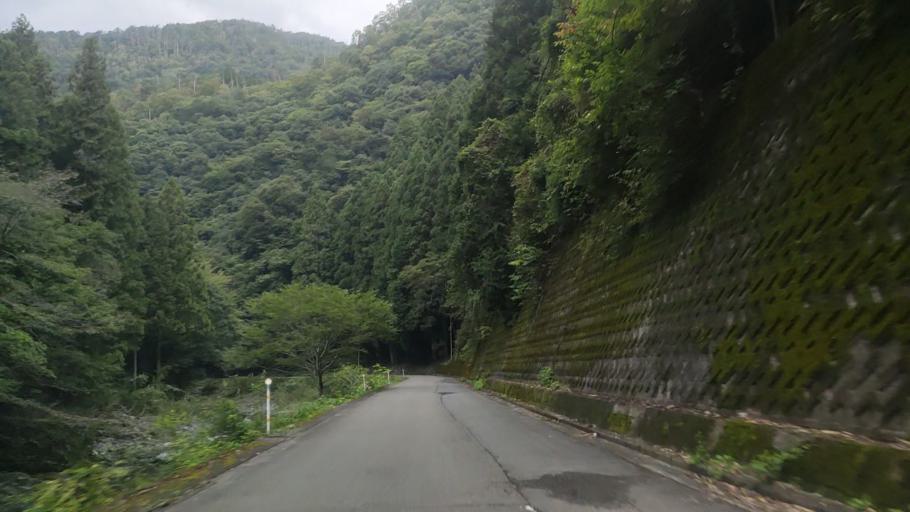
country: JP
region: Wakayama
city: Hashimoto
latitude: 34.2690
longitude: 135.6403
